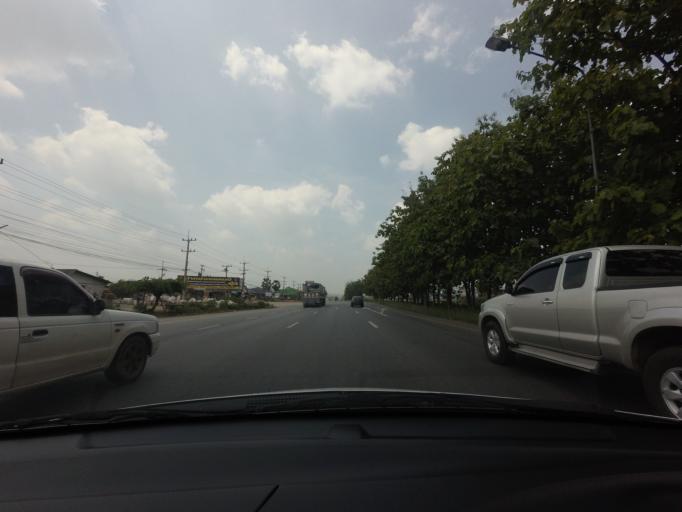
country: TH
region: Nakhon Ratchasima
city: Pak Chong
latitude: 14.6661
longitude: 101.4291
